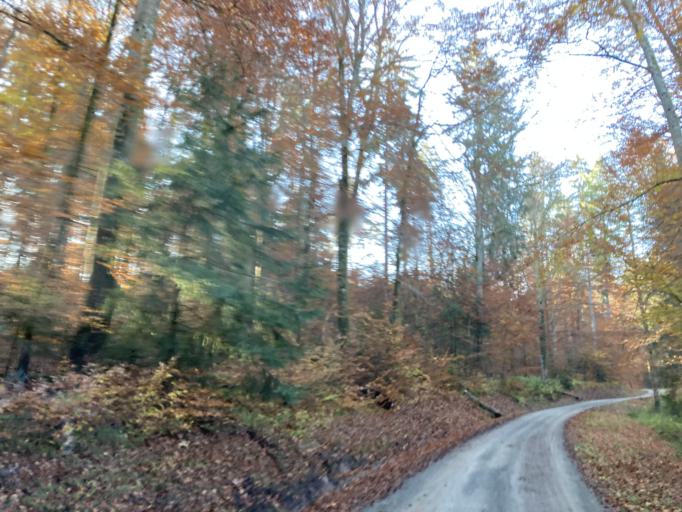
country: DE
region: Baden-Wuerttemberg
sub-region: Tuebingen Region
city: Tuebingen
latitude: 48.5388
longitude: 9.0001
